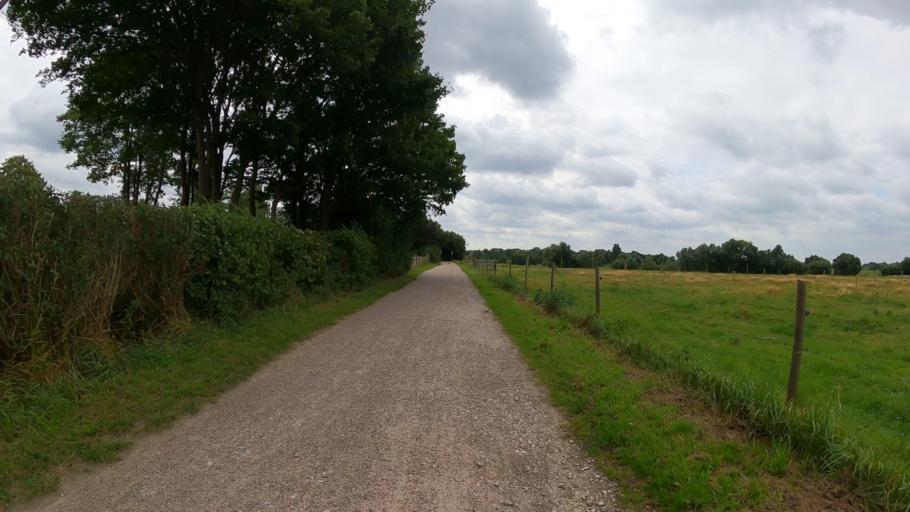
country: DE
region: Lower Saxony
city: Neu Wulmstorf
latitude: 53.5254
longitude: 9.8441
